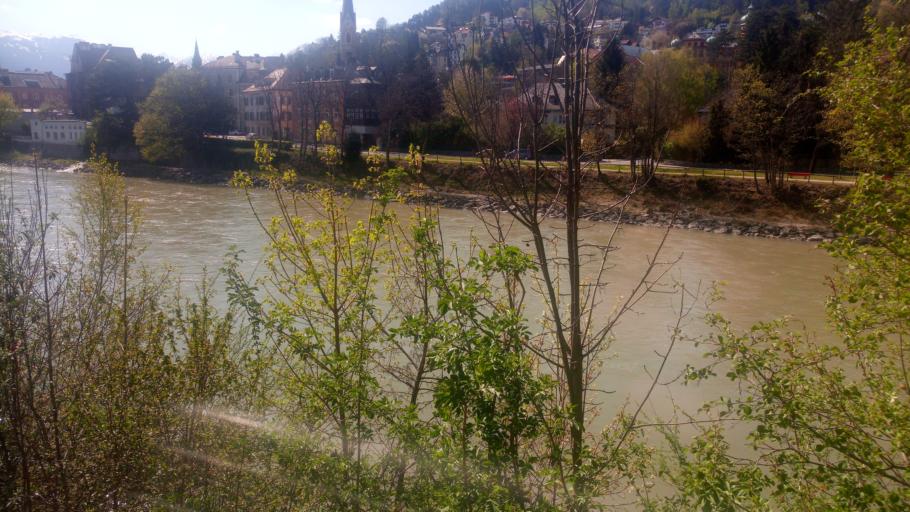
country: AT
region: Tyrol
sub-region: Innsbruck Stadt
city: Innsbruck
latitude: 47.2738
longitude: 11.3961
